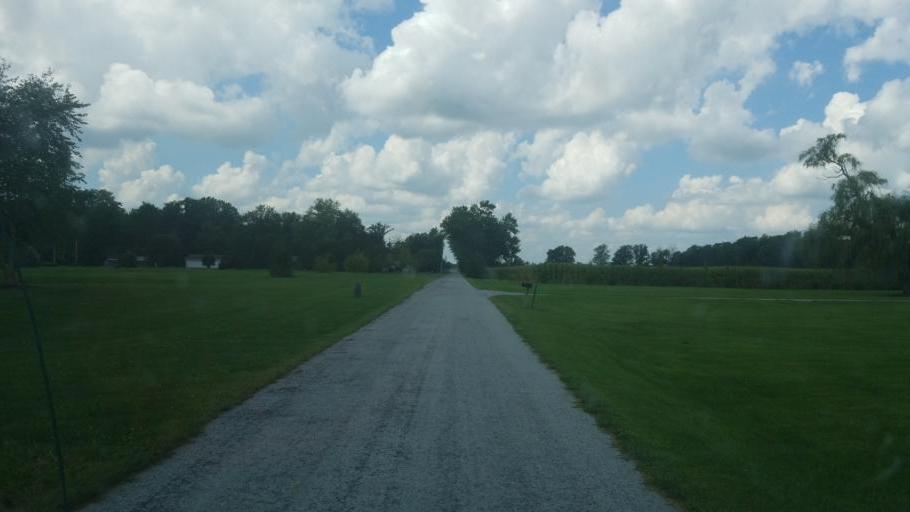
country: US
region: Ohio
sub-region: Hardin County
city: Kenton
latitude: 40.6879
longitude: -83.5616
